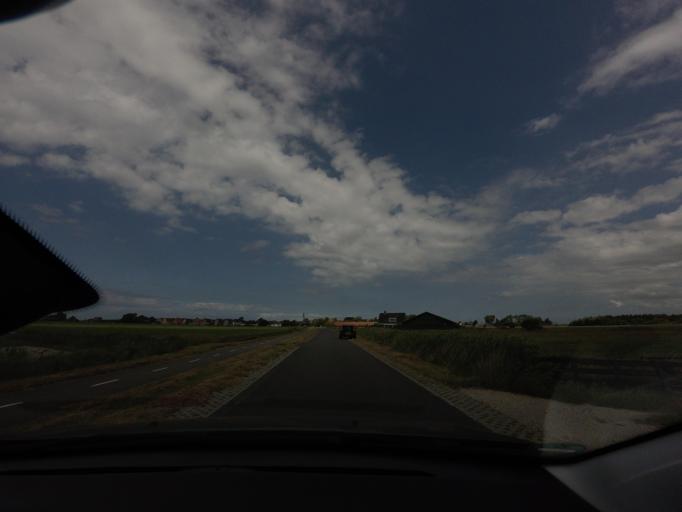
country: NL
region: North Holland
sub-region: Gemeente Texel
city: Den Burg
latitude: 53.0209
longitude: 4.7578
